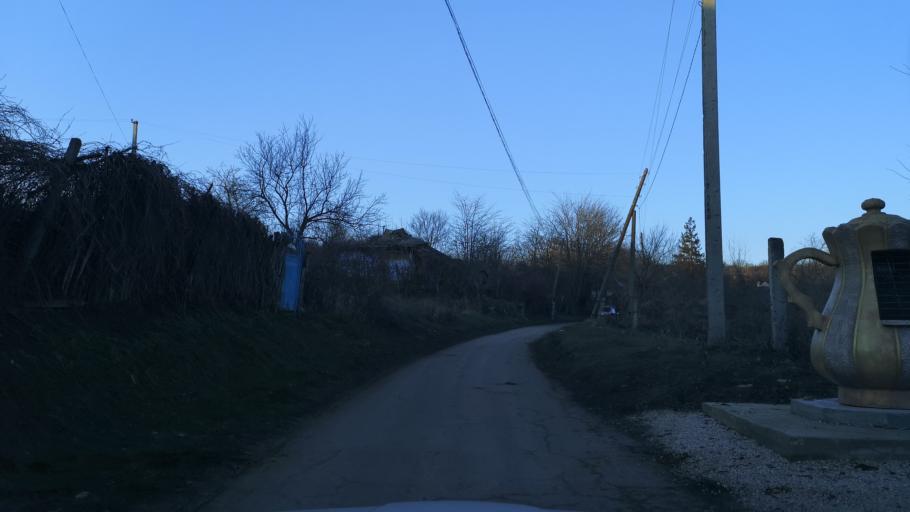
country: MD
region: Orhei
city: Orhei
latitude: 47.3667
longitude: 28.6902
